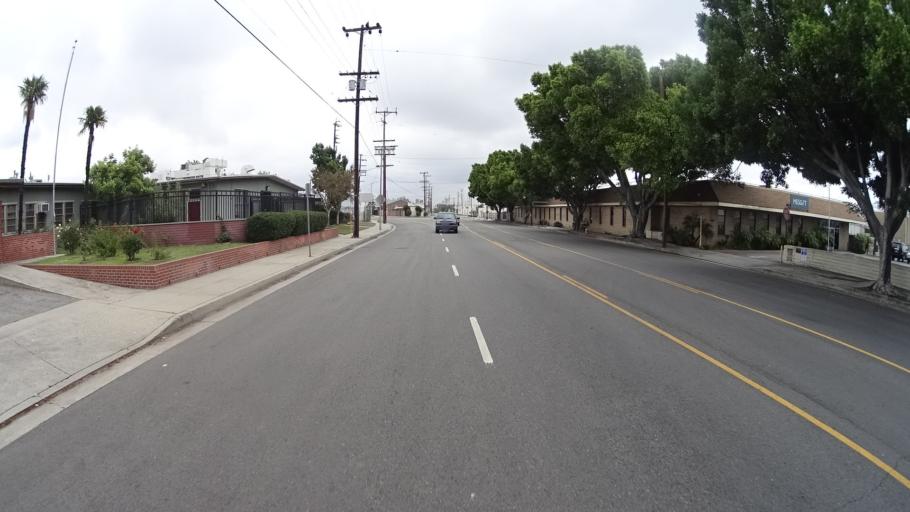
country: US
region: California
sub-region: Los Angeles County
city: Van Nuys
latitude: 34.2063
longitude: -118.4126
